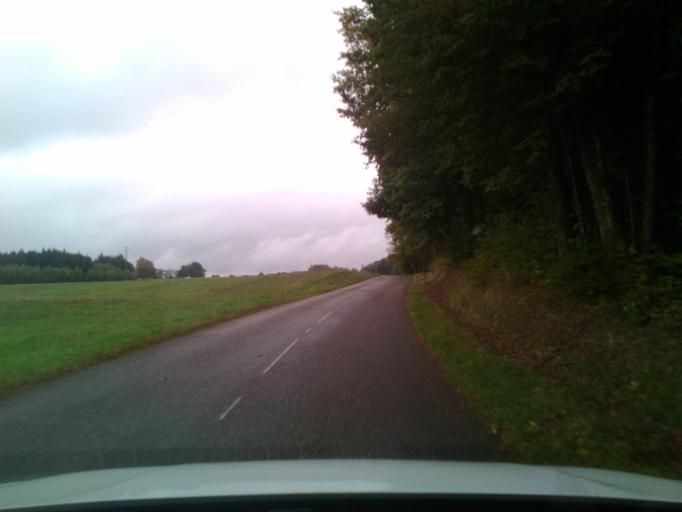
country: FR
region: Lorraine
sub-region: Departement des Vosges
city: Senones
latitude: 48.3669
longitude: 6.9639
